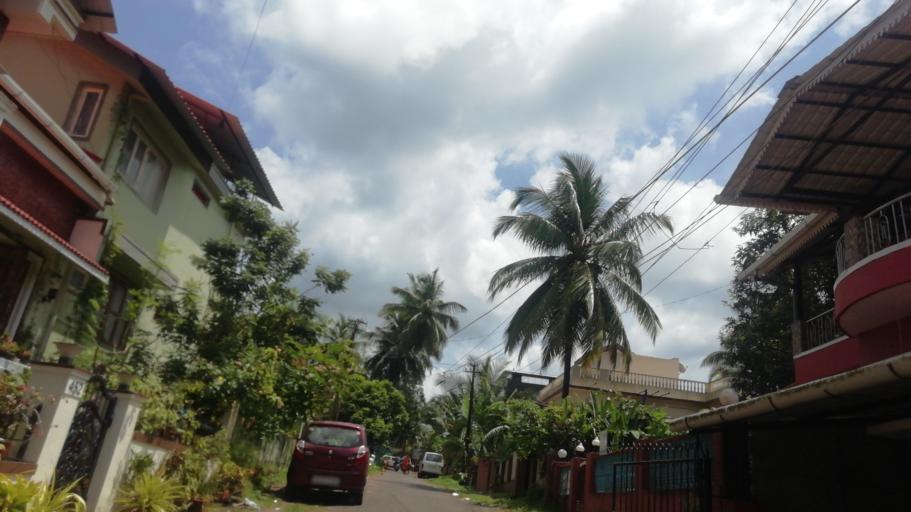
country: IN
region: Goa
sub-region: North Goa
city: Queula
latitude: 15.3863
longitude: 74.0013
